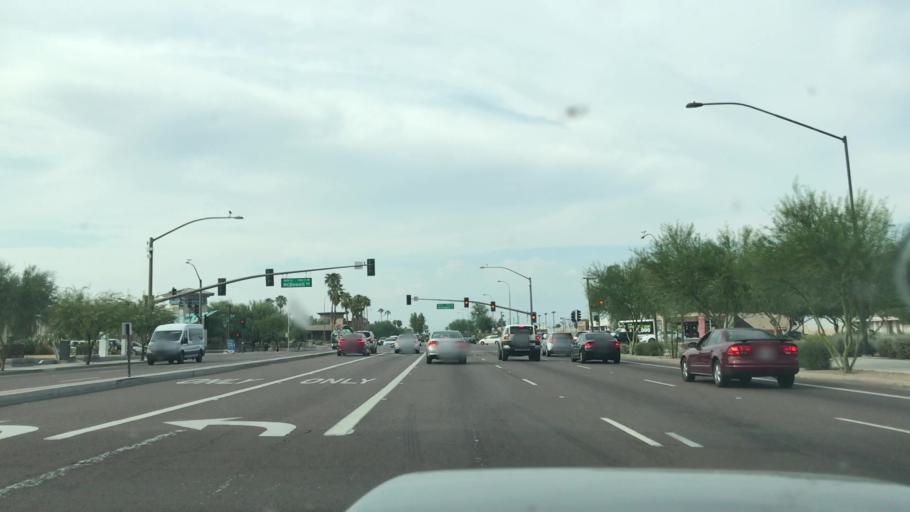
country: US
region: Arizona
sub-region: Maricopa County
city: Scottsdale
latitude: 33.4649
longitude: -111.9262
